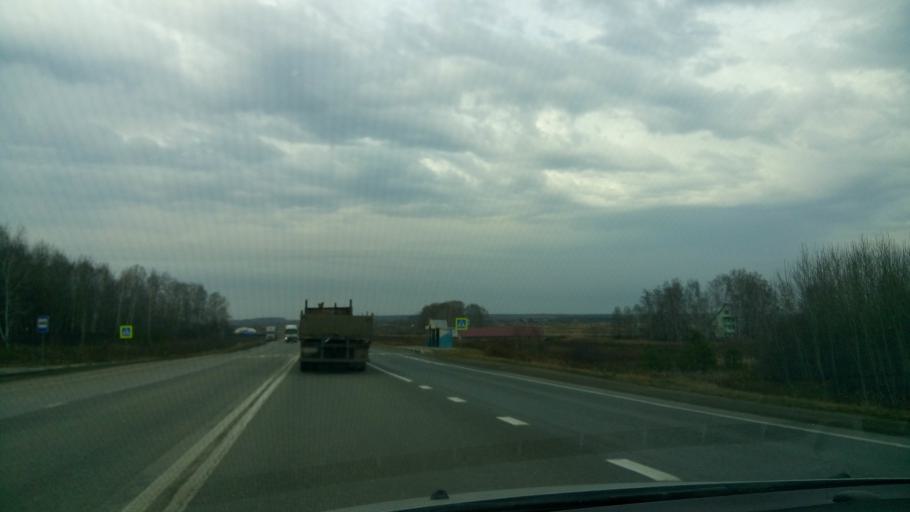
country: RU
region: Sverdlovsk
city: Kamyshlov
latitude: 56.8691
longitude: 62.7476
